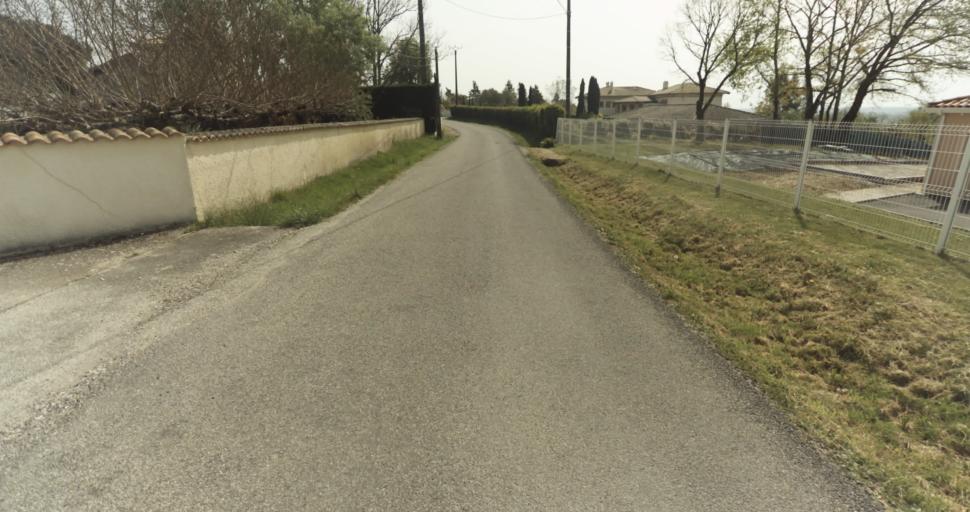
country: FR
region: Midi-Pyrenees
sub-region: Departement du Tarn-et-Garonne
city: Moissac
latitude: 44.1072
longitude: 1.0762
